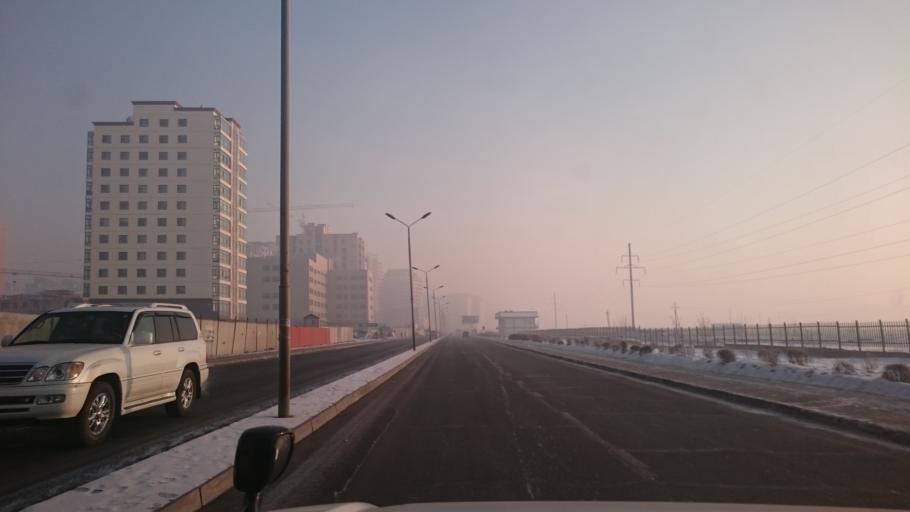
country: MN
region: Ulaanbaatar
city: Ulaanbaatar
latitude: 47.9009
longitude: 106.9350
